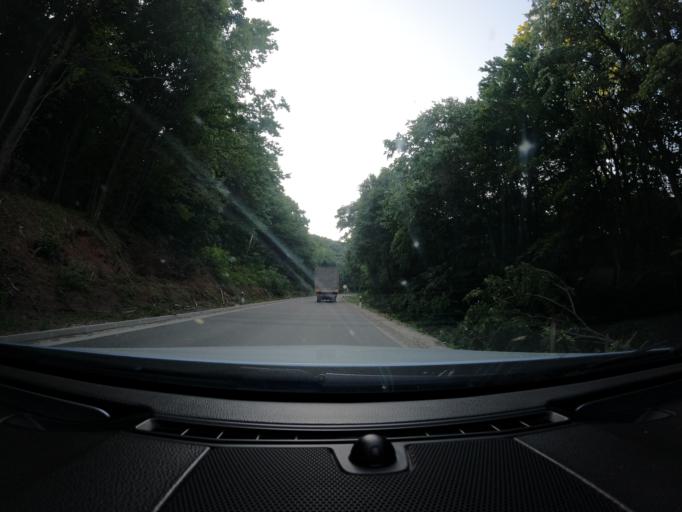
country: RS
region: Autonomna Pokrajina Vojvodina
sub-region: Juznobacki Okrug
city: Beocin
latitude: 45.1497
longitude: 19.7153
